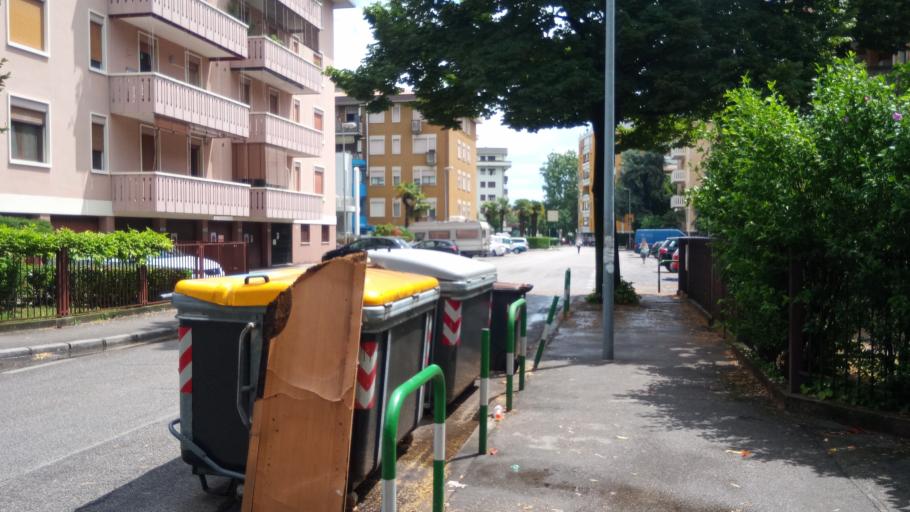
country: IT
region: Veneto
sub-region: Provincia di Padova
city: Padova
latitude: 45.4291
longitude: 11.8940
